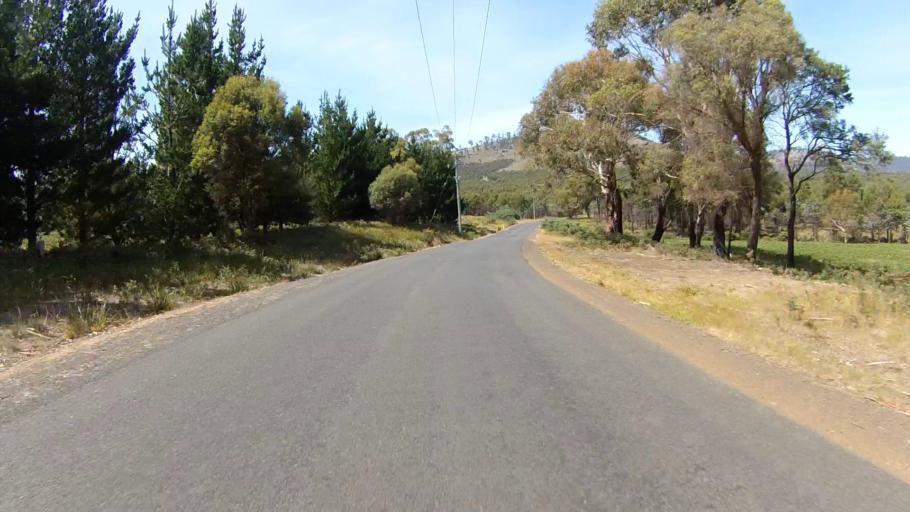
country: AU
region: Tasmania
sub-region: Sorell
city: Sorell
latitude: -42.6170
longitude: 147.7301
